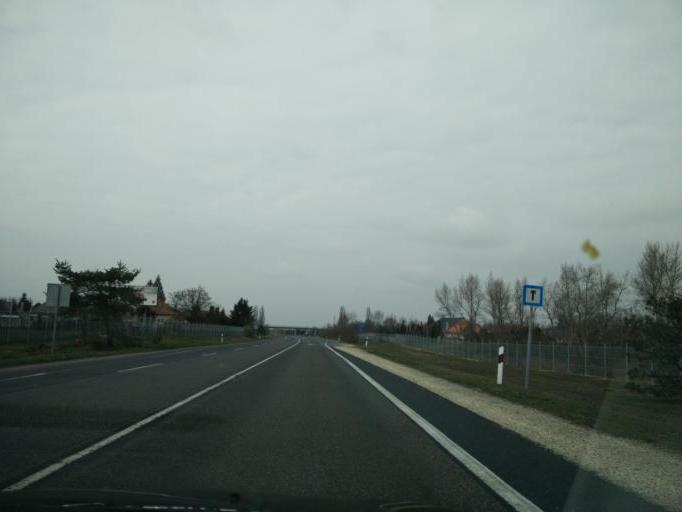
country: HU
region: Gyor-Moson-Sopron
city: Toltestava
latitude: 47.7129
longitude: 17.7382
